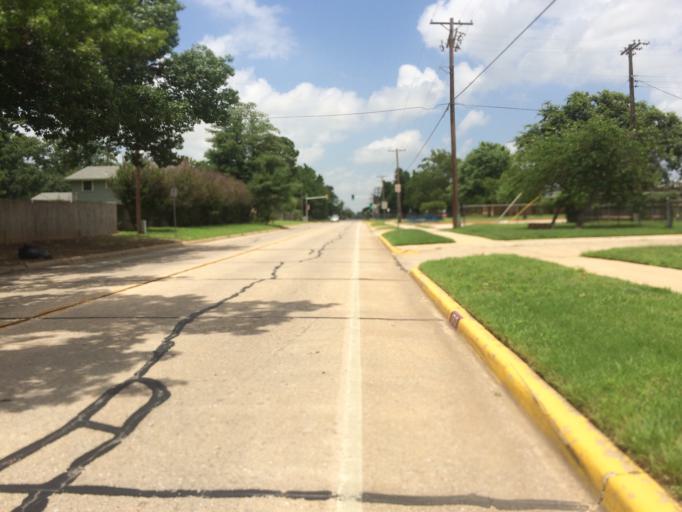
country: US
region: Oklahoma
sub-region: Cleveland County
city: Norman
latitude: 35.1973
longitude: -97.4679
